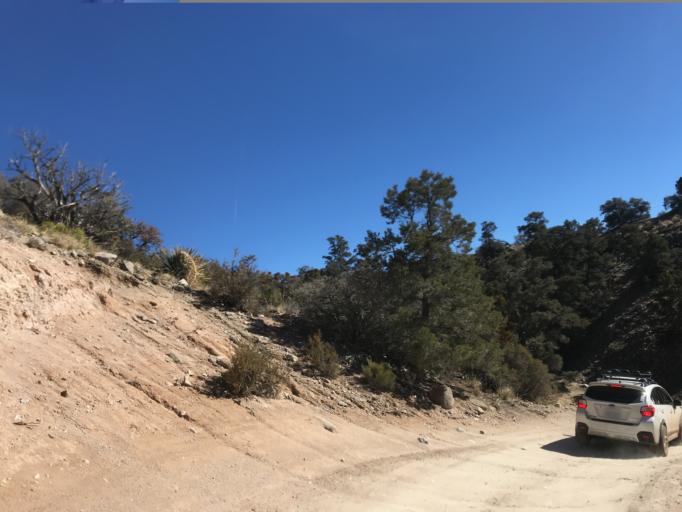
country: US
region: California
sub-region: San Bernardino County
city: Big Bear City
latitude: 34.2334
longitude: -116.6832
